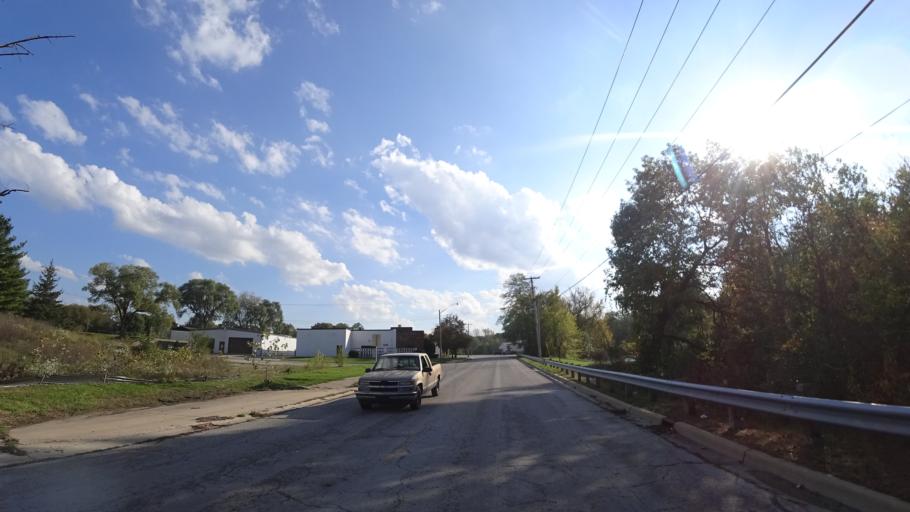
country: US
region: Michigan
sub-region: Saint Joseph County
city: Three Rivers
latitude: 41.9516
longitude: -85.6246
